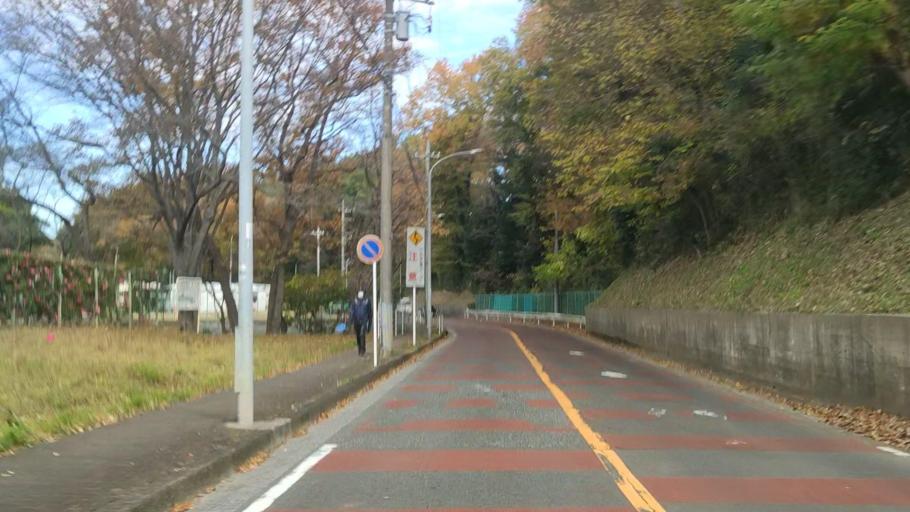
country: JP
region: Kanagawa
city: Yokohama
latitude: 35.4390
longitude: 139.5441
